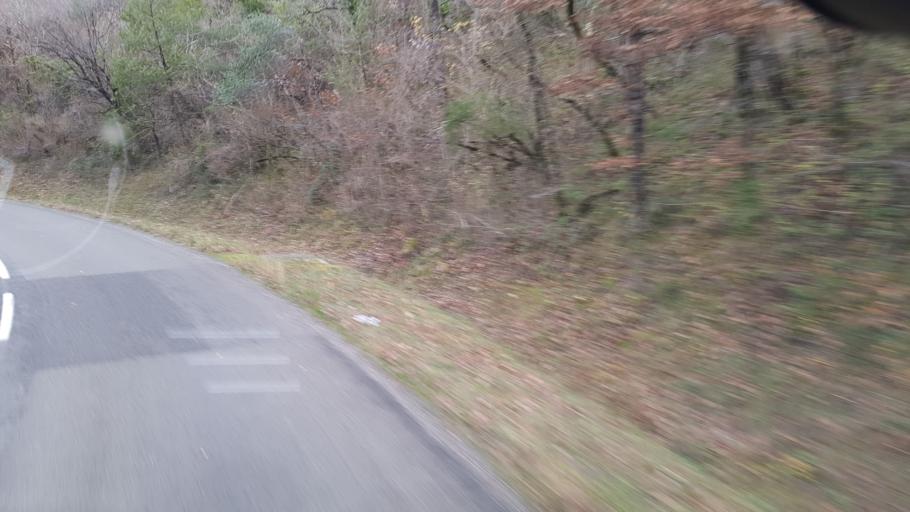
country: FR
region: Midi-Pyrenees
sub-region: Departement du Tarn-et-Garonne
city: Montricoux
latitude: 44.0174
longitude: 1.6778
